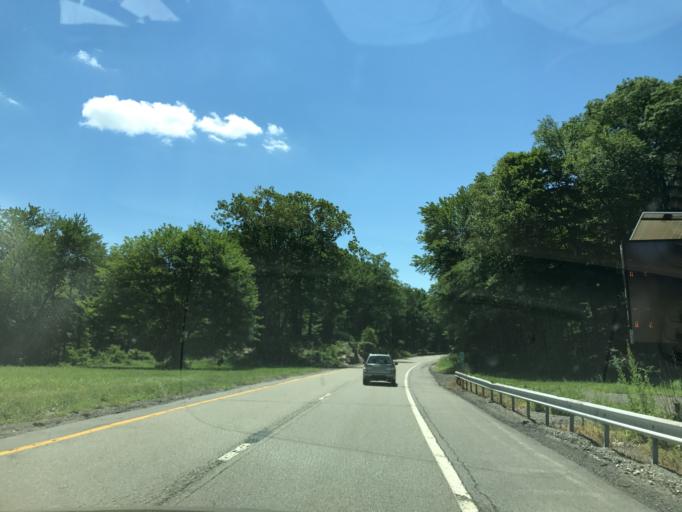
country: US
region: New York
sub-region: Dutchess County
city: Brinckerhoff
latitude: 41.4515
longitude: -73.8180
